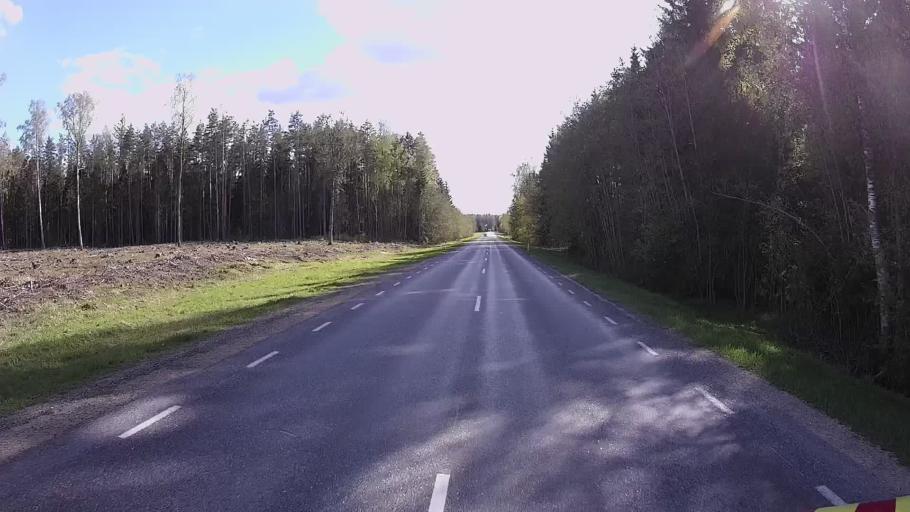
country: EE
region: Jogevamaa
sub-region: Jogeva linn
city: Jogeva
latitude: 58.7437
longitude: 26.3051
